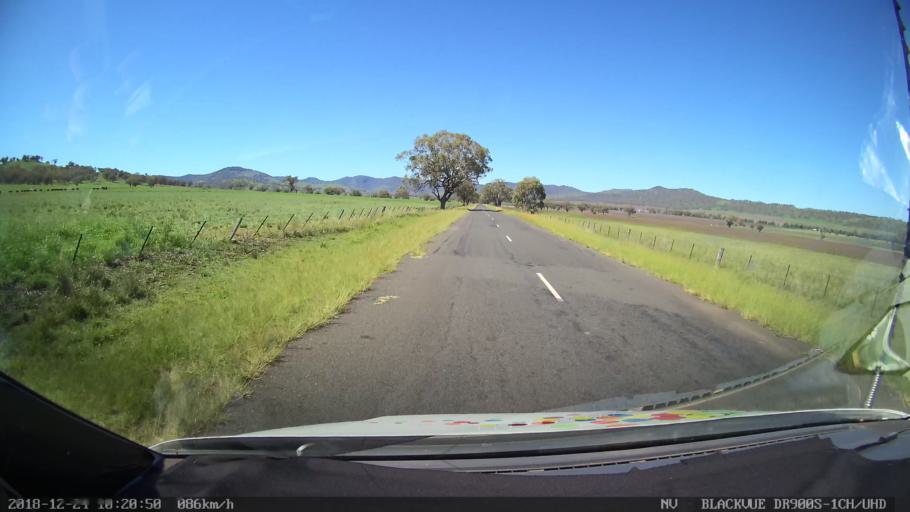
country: AU
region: New South Wales
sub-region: Liverpool Plains
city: Quirindi
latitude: -31.7452
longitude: 150.5548
